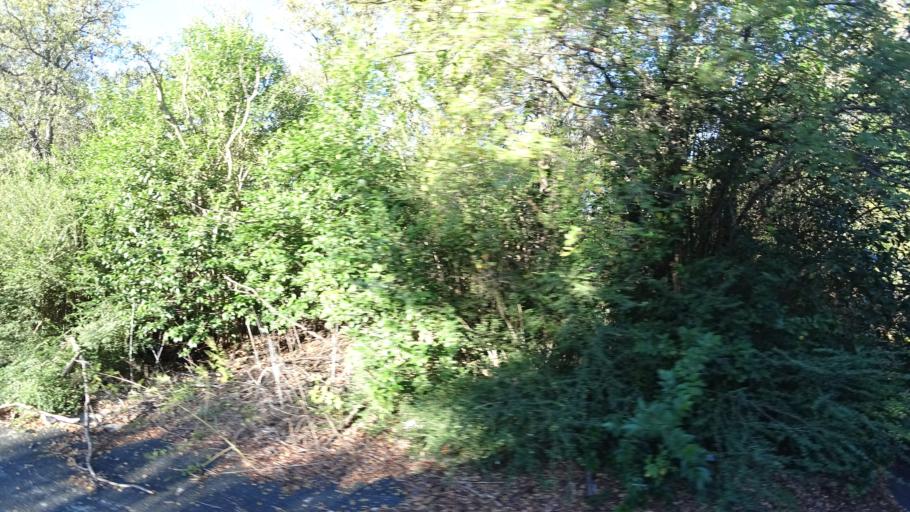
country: US
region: Texas
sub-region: Travis County
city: Austin
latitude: 30.2935
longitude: -97.6862
